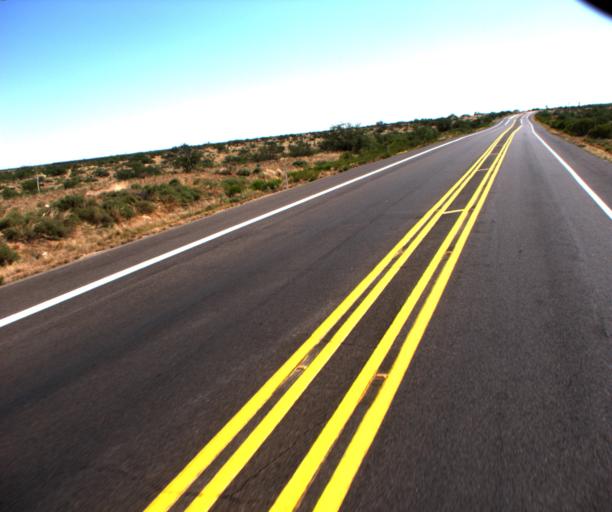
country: US
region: Arizona
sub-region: Pima County
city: Catalina
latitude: 32.5917
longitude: -110.8921
